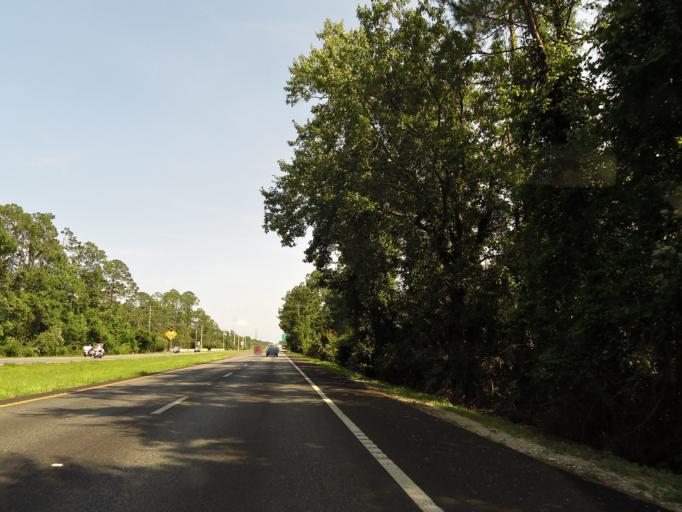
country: US
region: Florida
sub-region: Saint Johns County
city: Palm Valley
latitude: 30.1086
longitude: -81.4832
